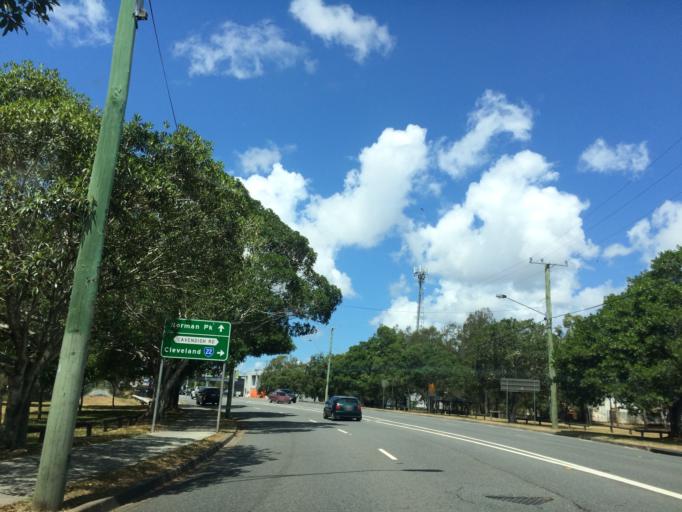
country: AU
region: Queensland
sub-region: Brisbane
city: Woolloongabba
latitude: -27.4878
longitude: 153.0522
